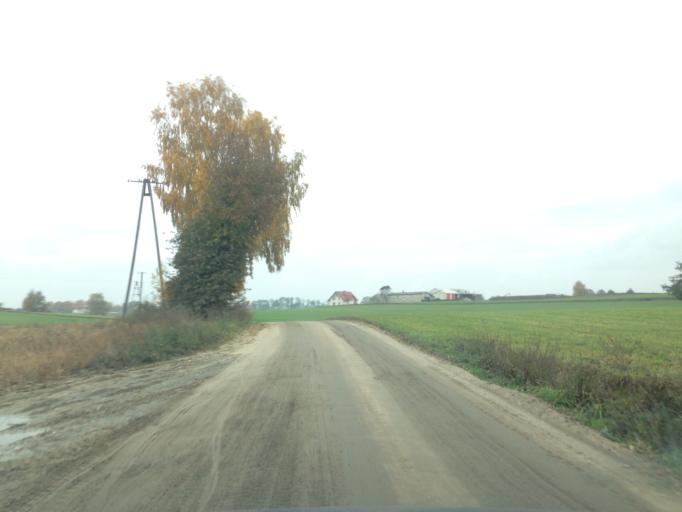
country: PL
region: Kujawsko-Pomorskie
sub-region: Powiat brodnicki
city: Brzozie
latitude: 53.3160
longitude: 19.7045
